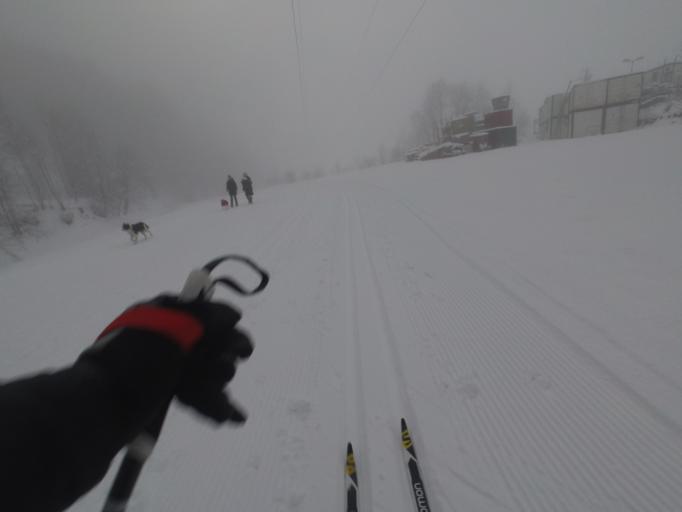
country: AT
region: Salzburg
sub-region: Politischer Bezirk Sankt Johann im Pongau
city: Wagrain
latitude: 47.3504
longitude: 13.3187
